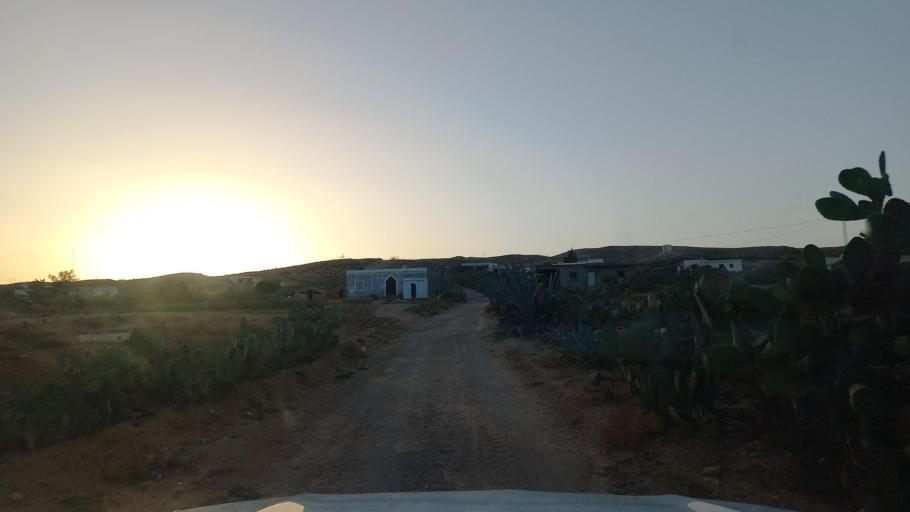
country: TN
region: Al Qasrayn
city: Sbiba
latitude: 35.3755
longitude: 9.0110
